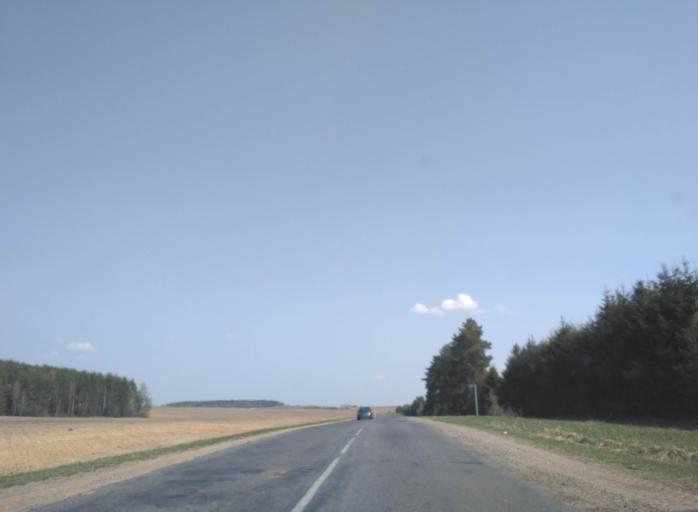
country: BY
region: Minsk
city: Horad Barysaw
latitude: 54.3085
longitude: 28.5404
